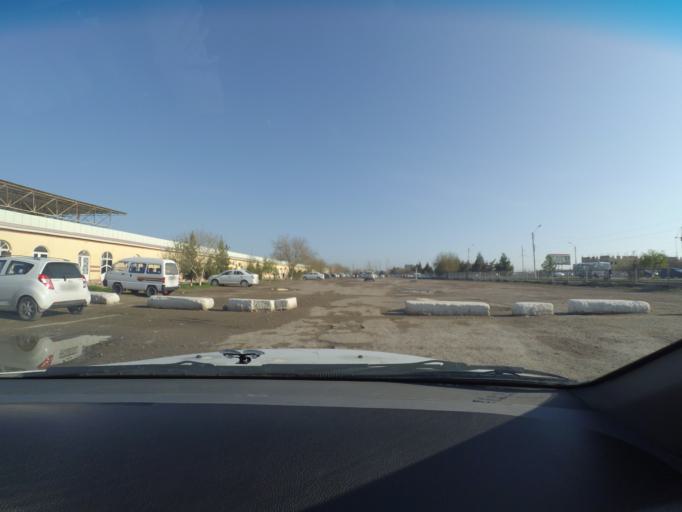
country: UZ
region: Bukhara
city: Bukhara
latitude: 39.8047
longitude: 64.4275
